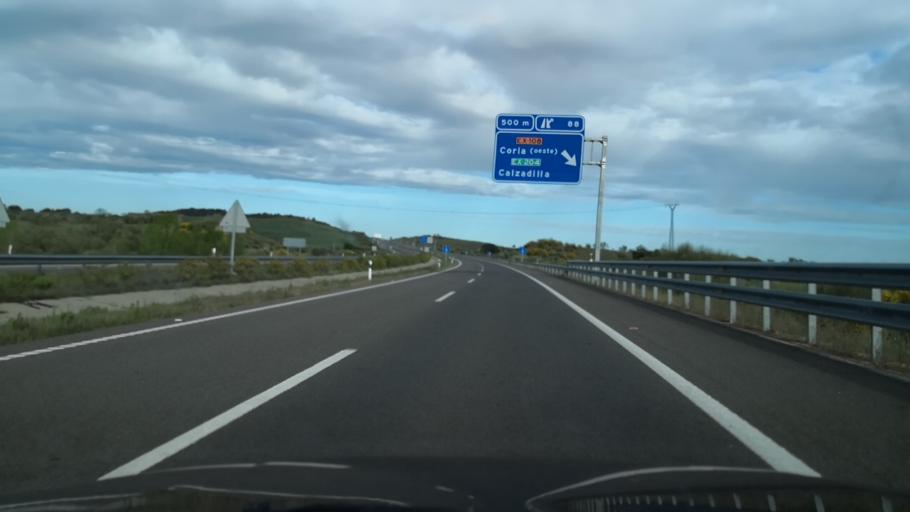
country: ES
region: Extremadura
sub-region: Provincia de Caceres
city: Casas de Don Gomez
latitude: 40.0115
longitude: -6.5737
